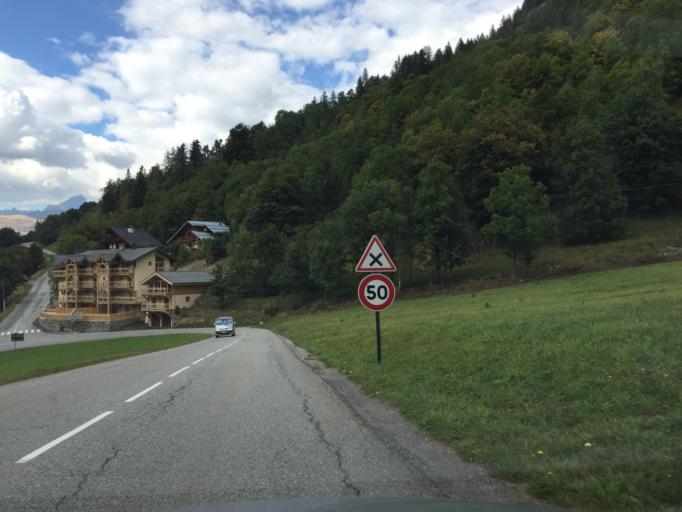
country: FR
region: Rhone-Alpes
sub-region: Departement de la Savoie
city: Belle-Plagne
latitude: 45.5373
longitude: 6.7650
